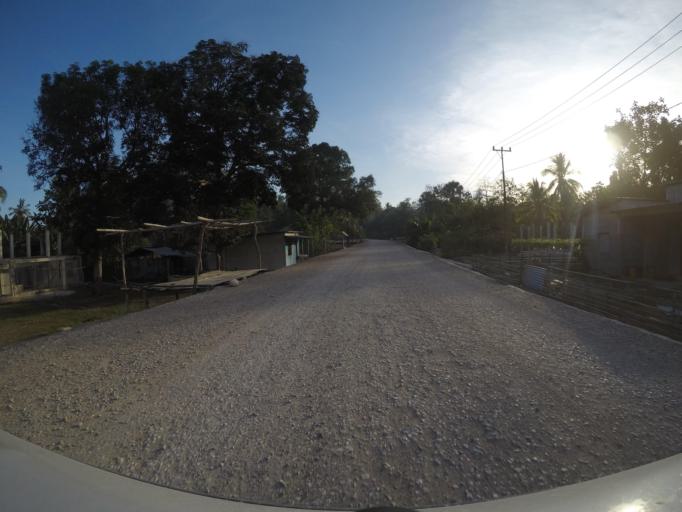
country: TL
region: Viqueque
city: Viqueque
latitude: -8.8427
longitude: 126.5121
